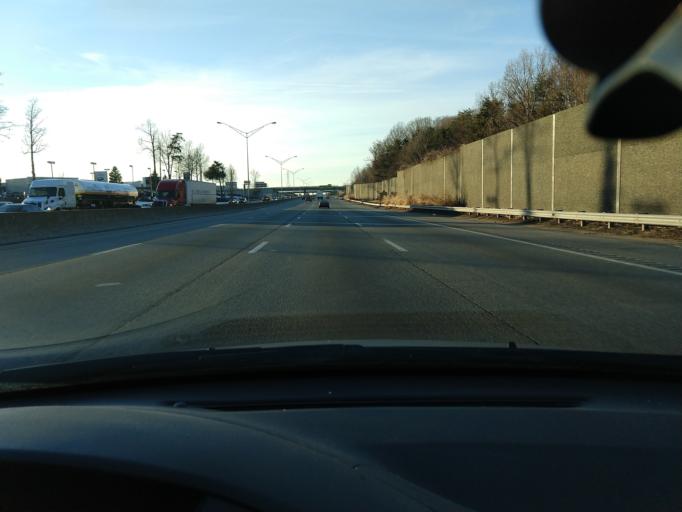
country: US
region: North Carolina
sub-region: Guilford County
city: Jamestown
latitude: 36.0594
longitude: -79.8986
